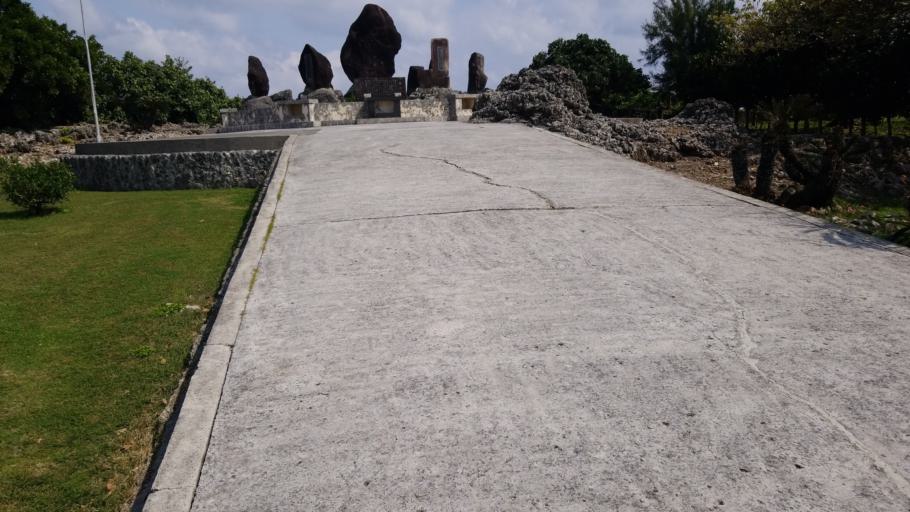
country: JP
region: Okinawa
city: Itoman
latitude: 26.0936
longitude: 127.7250
